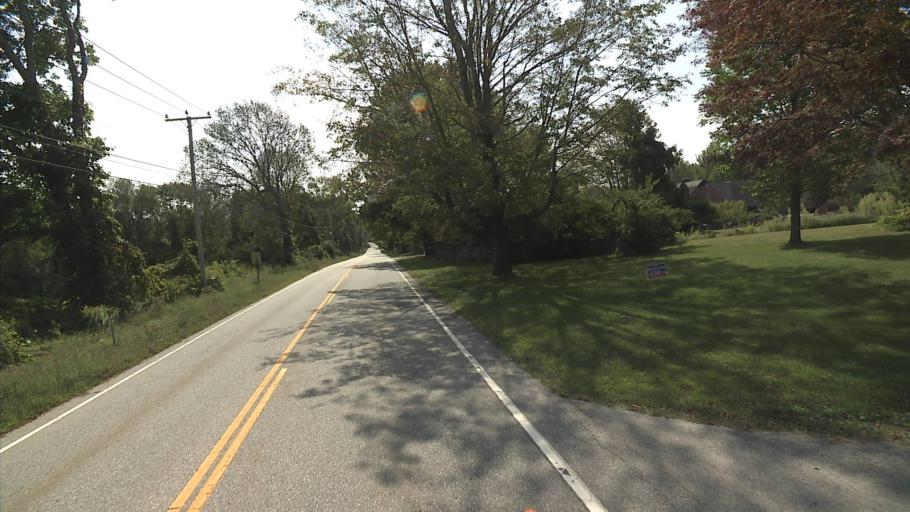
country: US
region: Connecticut
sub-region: Windham County
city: East Brooklyn
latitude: 41.8138
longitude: -71.9566
